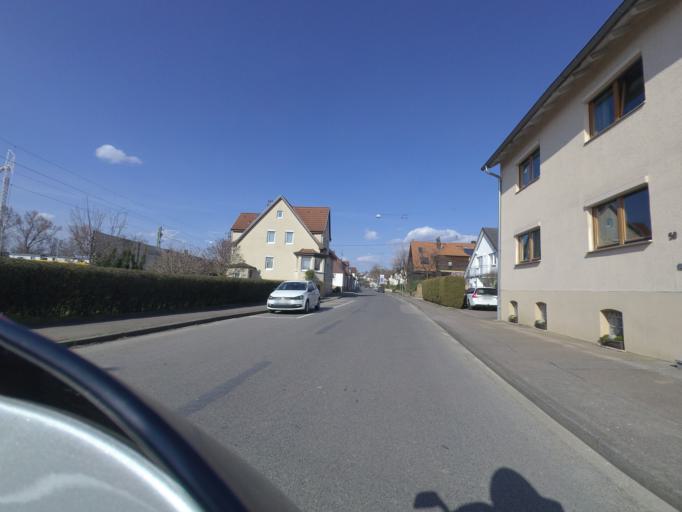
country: DE
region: Baden-Wuerttemberg
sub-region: Regierungsbezirk Stuttgart
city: Oberboihingen
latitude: 48.6526
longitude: 9.3654
